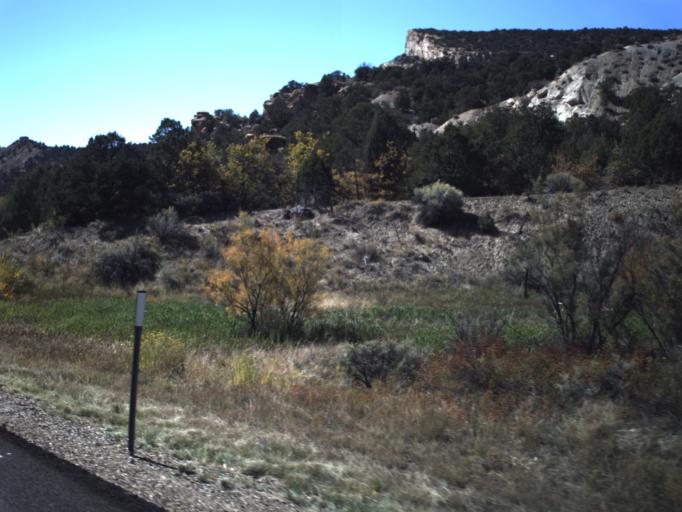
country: US
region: Utah
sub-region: Garfield County
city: Panguitch
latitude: 37.6053
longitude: -111.9089
